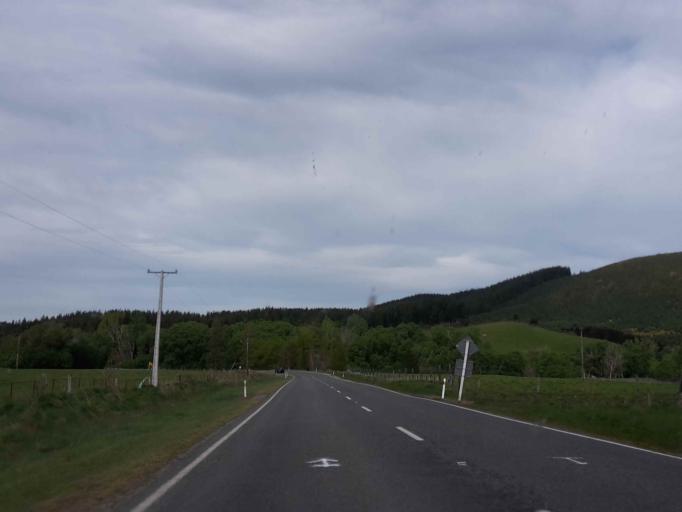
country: NZ
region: Canterbury
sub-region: Timaru District
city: Pleasant Point
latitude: -44.1228
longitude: 171.0419
